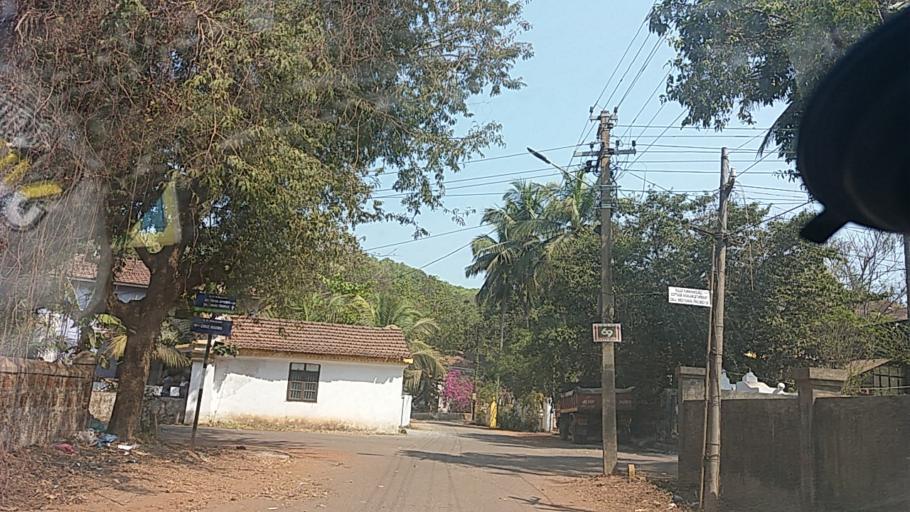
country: IN
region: Goa
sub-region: North Goa
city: Saligao
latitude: 15.5376
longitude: 73.7865
